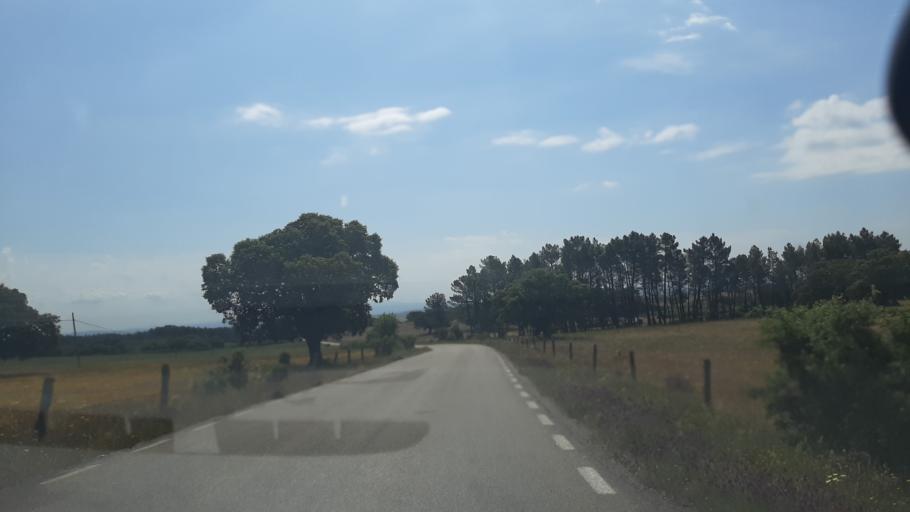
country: ES
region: Castille and Leon
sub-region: Provincia de Salamanca
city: Gallegos de Arganan
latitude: 40.6435
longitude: -6.7420
